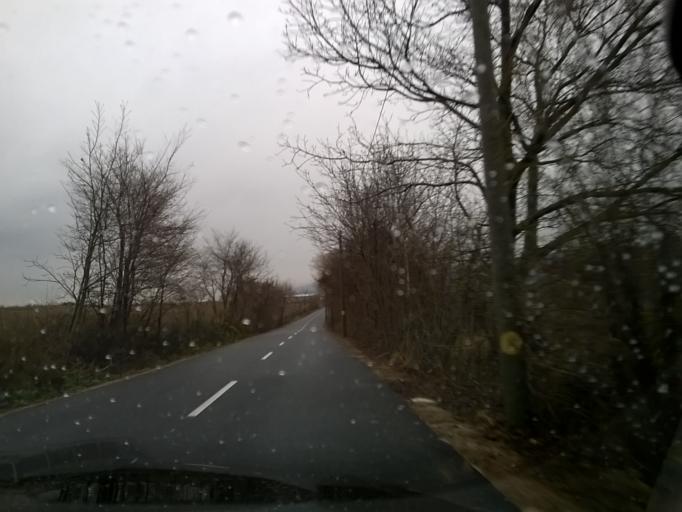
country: SK
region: Nitriansky
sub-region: Okres Nitra
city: Nitra
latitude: 48.3352
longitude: 18.0226
